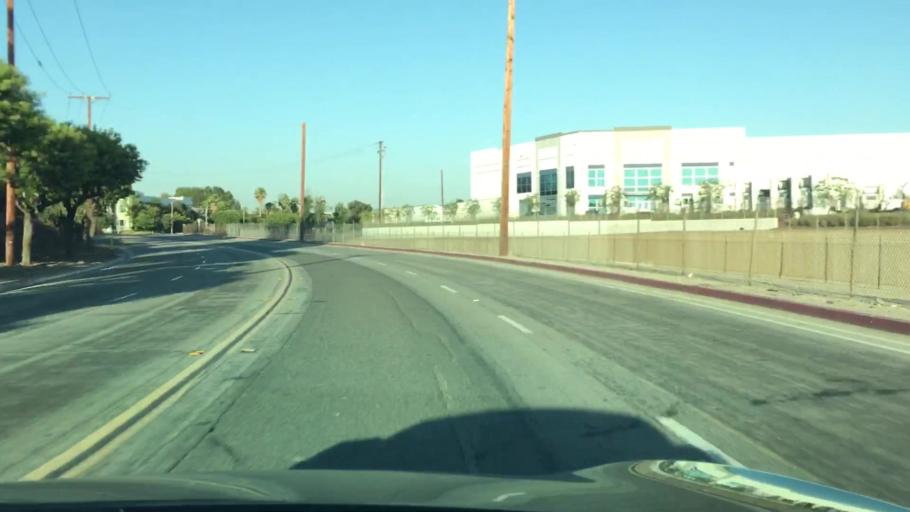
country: US
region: California
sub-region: Los Angeles County
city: South San Jose Hills
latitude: 34.0045
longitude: -117.9173
